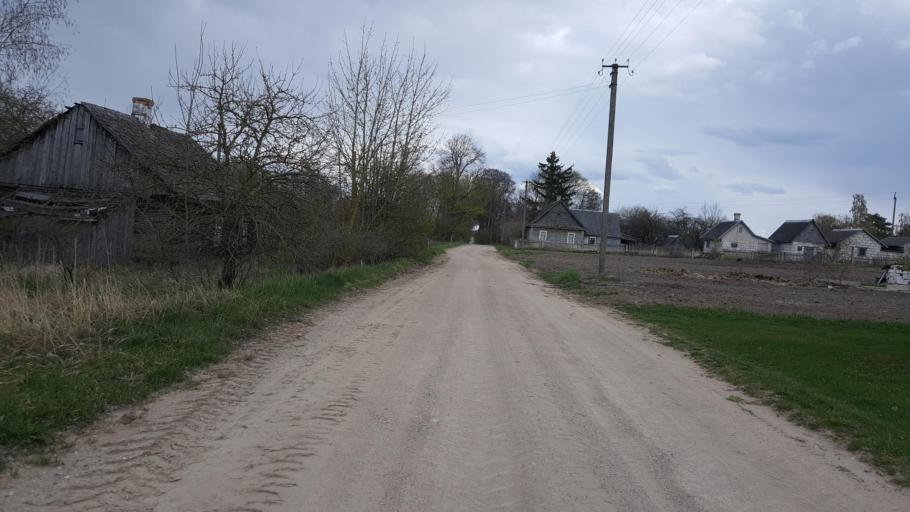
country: BY
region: Brest
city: Kamyanyets
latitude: 52.4067
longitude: 23.7118
